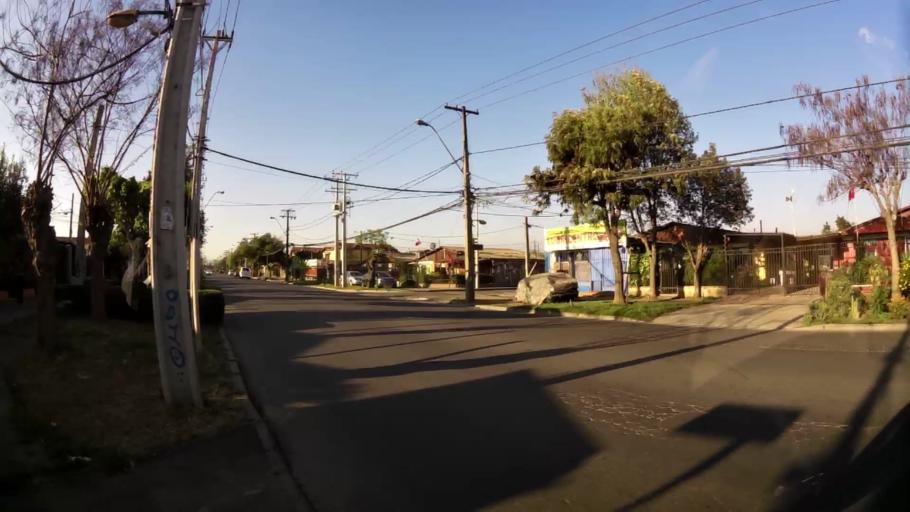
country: CL
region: Santiago Metropolitan
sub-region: Provincia de Santiago
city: Lo Prado
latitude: -33.4782
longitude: -70.7493
